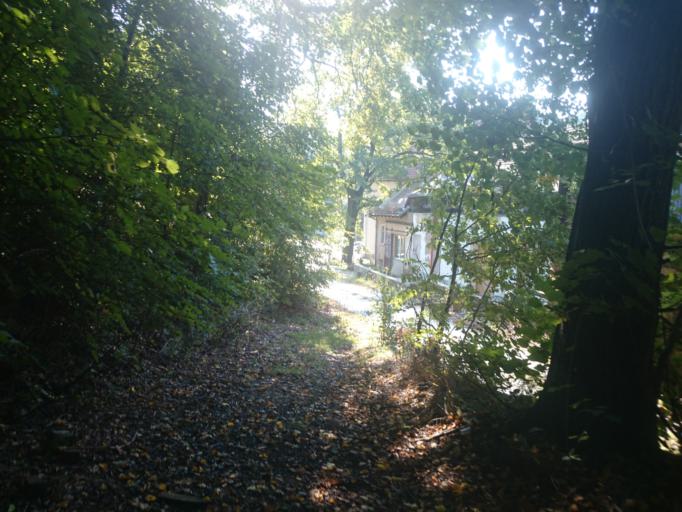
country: DE
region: Saxony
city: Kreischa
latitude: 50.9844
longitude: 13.7977
